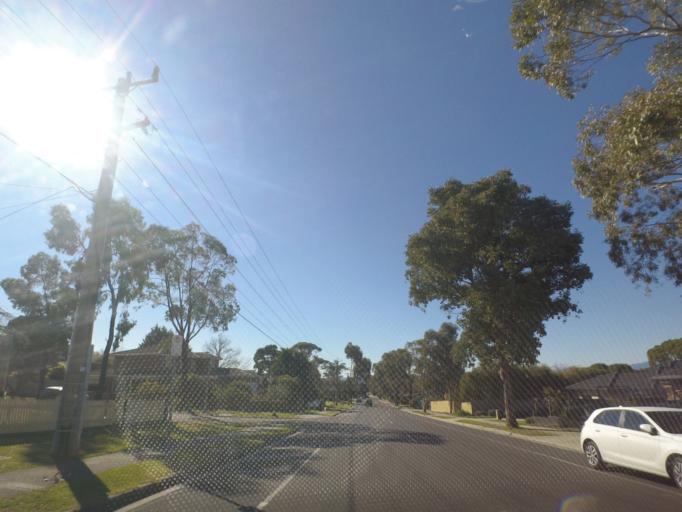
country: AU
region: Victoria
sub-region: Maroondah
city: Croydon Hills
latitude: -37.7802
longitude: 145.2562
